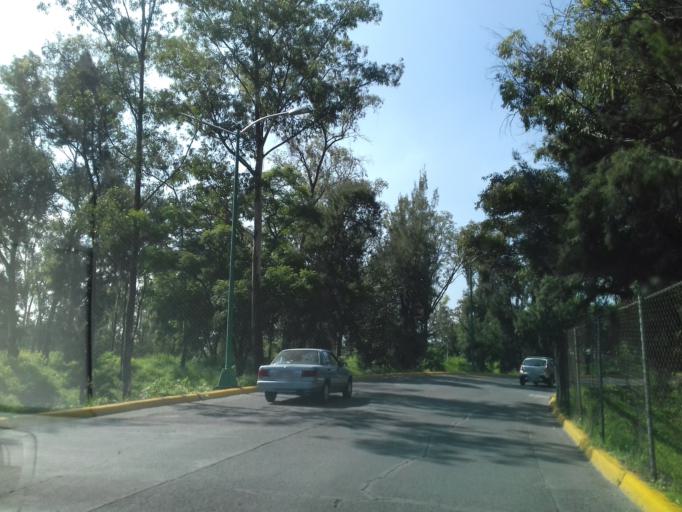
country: MX
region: Mexico City
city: Magdalena Contreras
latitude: 19.3284
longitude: -99.1898
